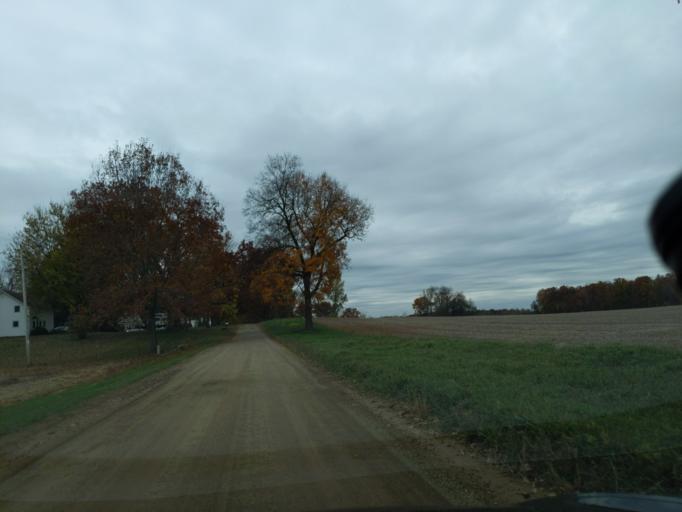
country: US
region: Michigan
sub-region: Eaton County
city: Eaton Rapids
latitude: 42.4340
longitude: -84.6005
